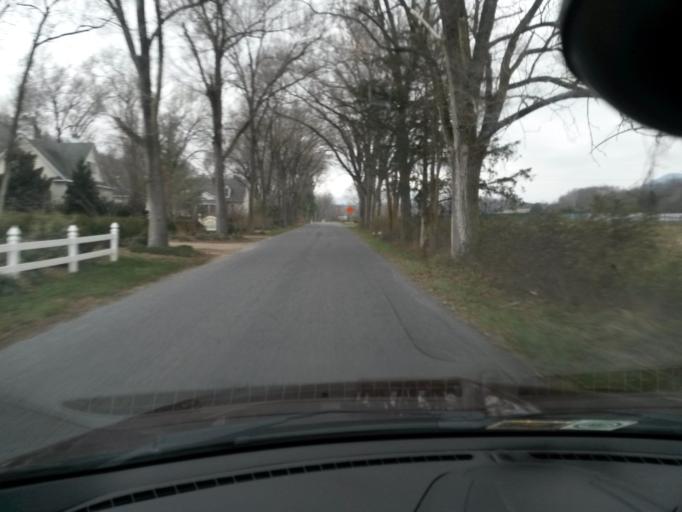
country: US
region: Virginia
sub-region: City of Lexington
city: Lexington
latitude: 37.8478
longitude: -79.4808
